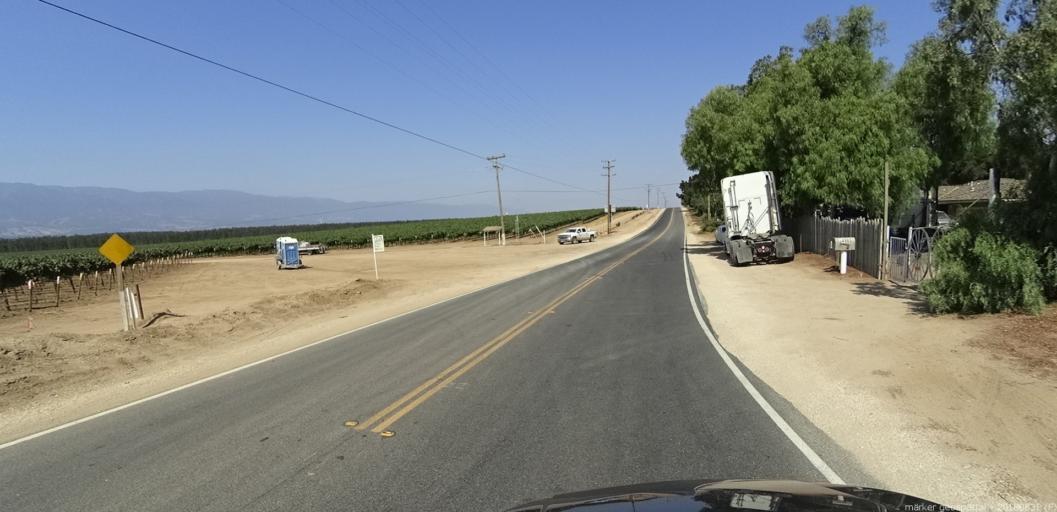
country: US
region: California
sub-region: Monterey County
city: Soledad
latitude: 36.4160
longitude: -121.2781
